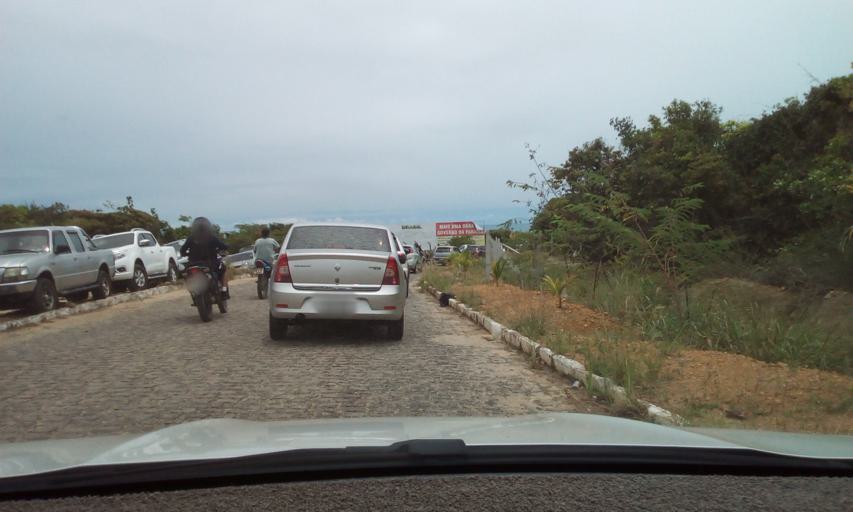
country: BR
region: Paraiba
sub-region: Conde
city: Conde
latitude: -7.3298
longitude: -34.7987
